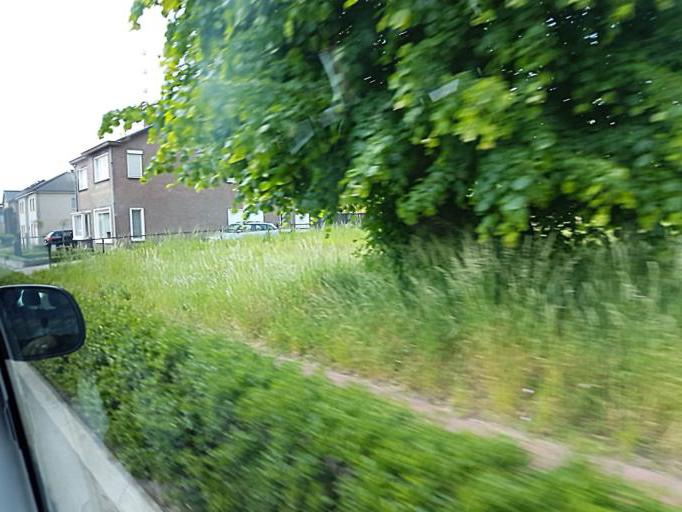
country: BE
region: Flanders
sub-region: Provincie Limburg
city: Neerpelt
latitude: 51.2289
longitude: 5.4737
